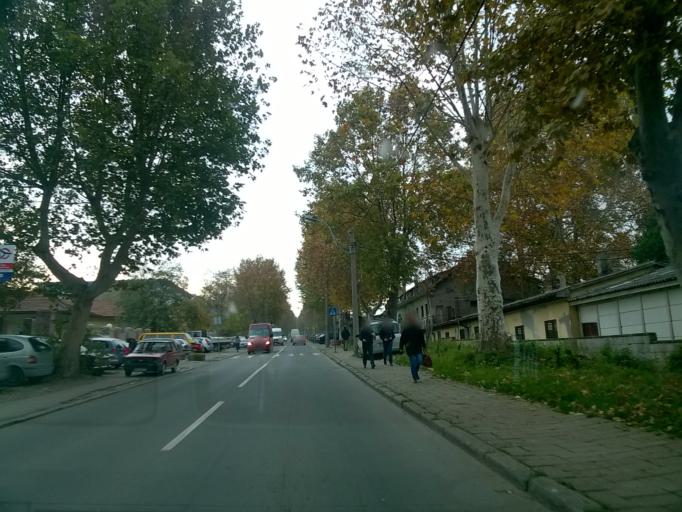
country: RS
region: Central Serbia
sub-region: Belgrade
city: Palilula
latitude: 44.8135
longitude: 20.4923
